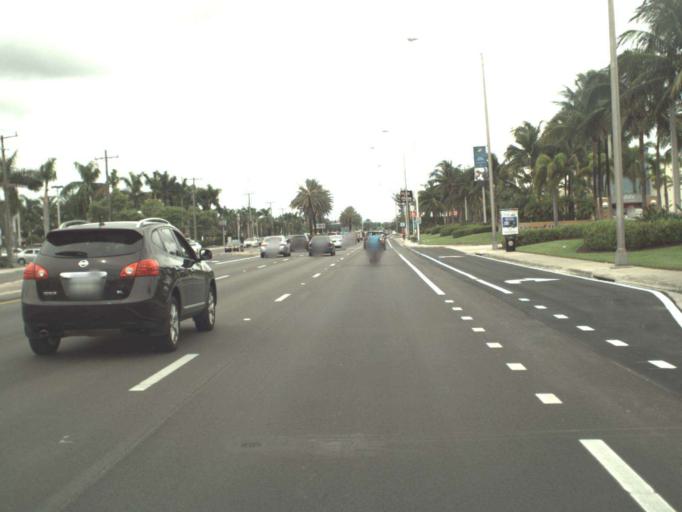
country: US
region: Florida
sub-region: Miami-Dade County
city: North Miami Beach
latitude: 25.9108
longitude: -80.1572
